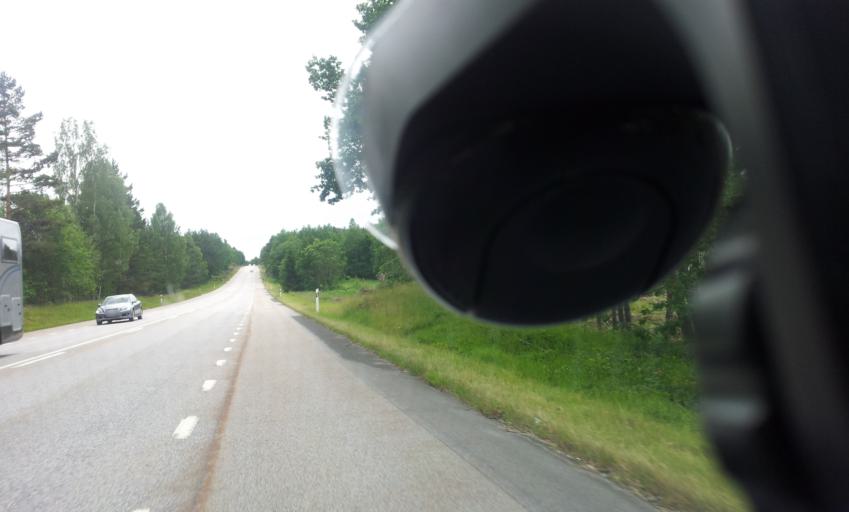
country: SE
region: Kalmar
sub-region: Vasterviks Kommun
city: Ankarsrum
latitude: 57.7039
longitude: 16.4447
